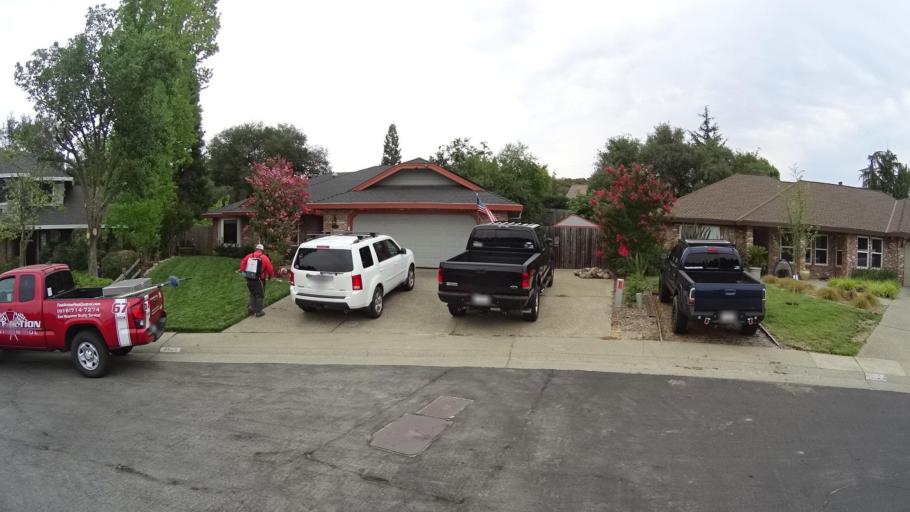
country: US
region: California
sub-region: Placer County
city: Rocklin
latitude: 38.7817
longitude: -121.2109
